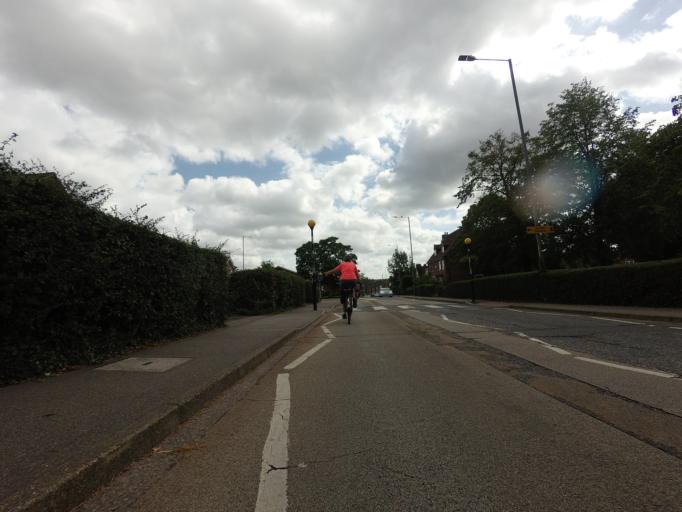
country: GB
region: England
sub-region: Kent
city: Sevenoaks
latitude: 51.2931
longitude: 0.1672
